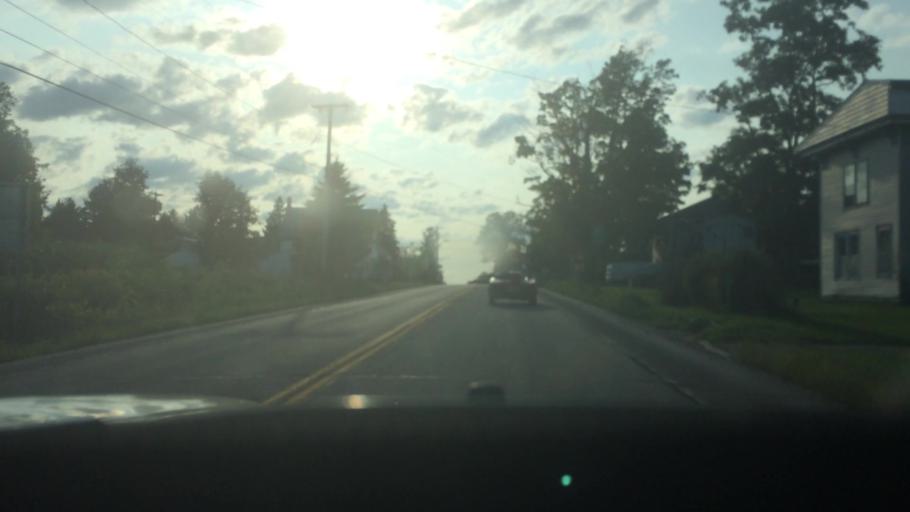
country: US
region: New York
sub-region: St. Lawrence County
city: Ogdensburg
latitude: 44.6653
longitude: -75.3562
